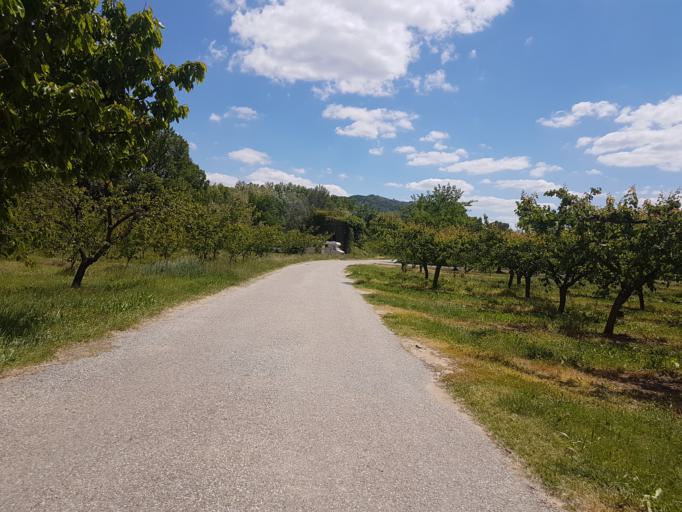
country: FR
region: Rhone-Alpes
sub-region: Departement de l'Ardeche
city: Saint-Jean-de-Muzols
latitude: 45.1018
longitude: 4.8217
